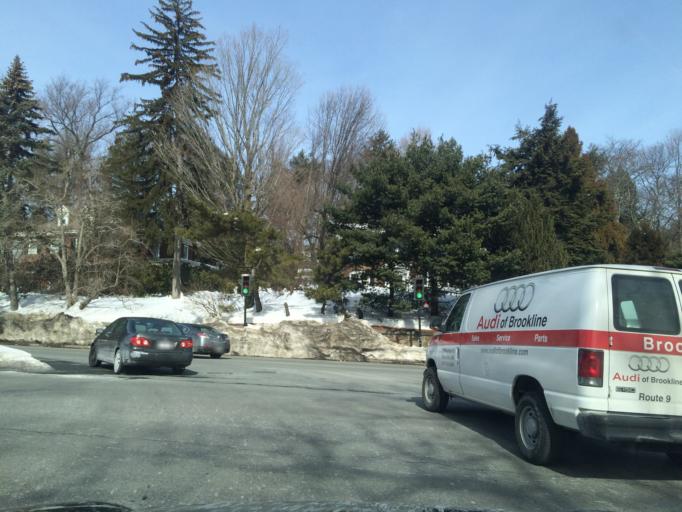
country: US
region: Massachusetts
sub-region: Norfolk County
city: Brookline
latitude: 42.3264
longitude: -71.1409
